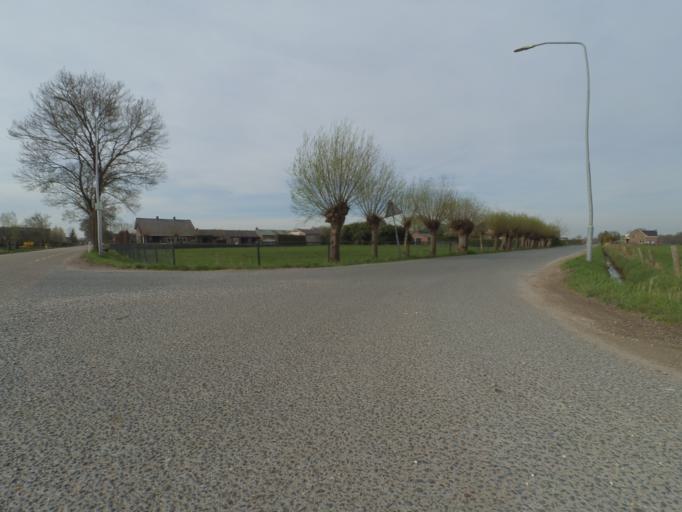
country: NL
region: Gelderland
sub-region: Gemeente Ede
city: Ederveen
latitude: 52.0549
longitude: 5.6070
